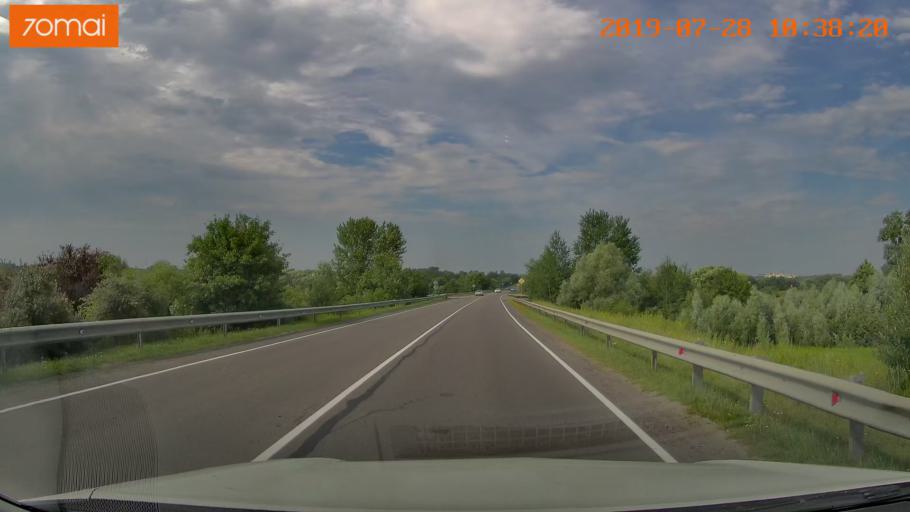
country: RU
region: Kaliningrad
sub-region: Gorod Kaliningrad
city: Kaliningrad
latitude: 54.7247
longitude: 20.4007
